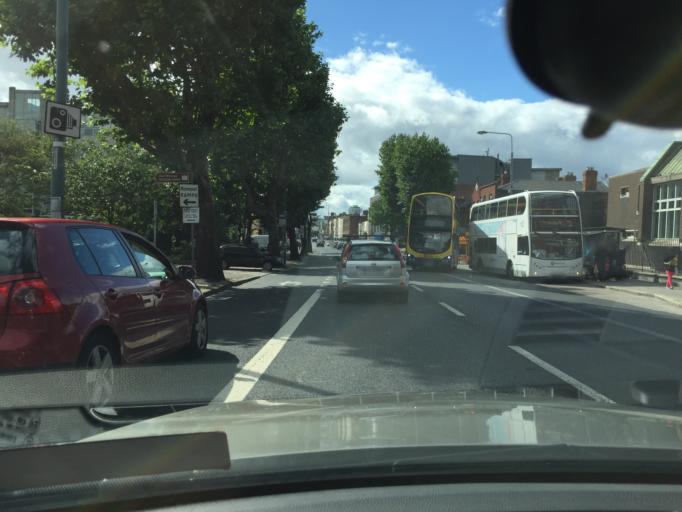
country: IE
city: Fairview
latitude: 53.3558
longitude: -6.2452
